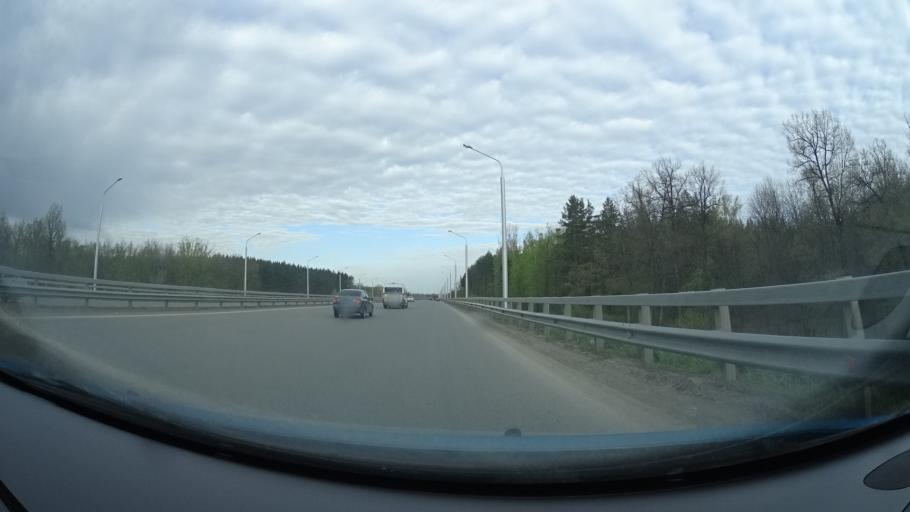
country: RU
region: Bashkortostan
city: Ufa
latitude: 54.7778
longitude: 55.9370
